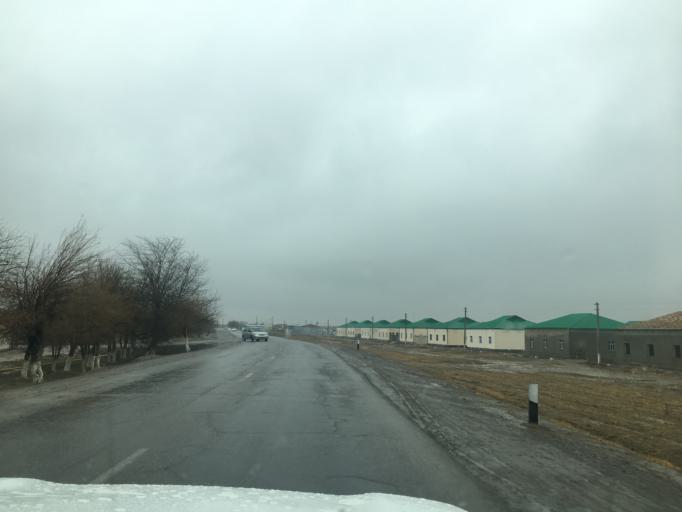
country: TM
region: Mary
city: Yoloeten
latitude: 37.2943
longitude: 62.3345
